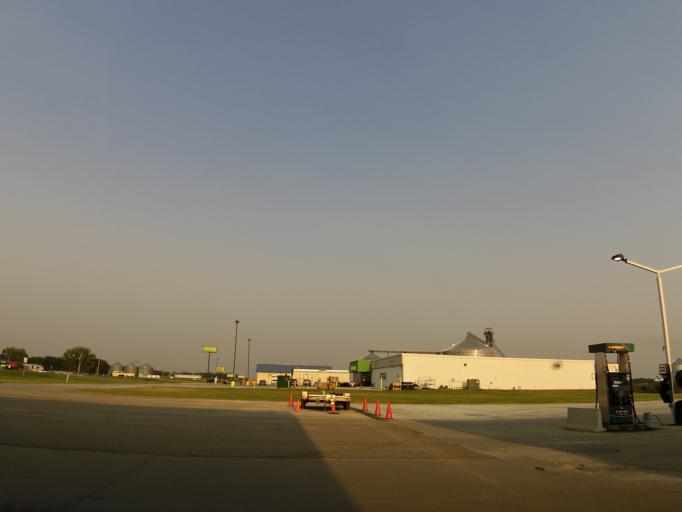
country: US
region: North Dakota
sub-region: Traill County
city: Mayville
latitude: 47.4976
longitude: -97.3121
